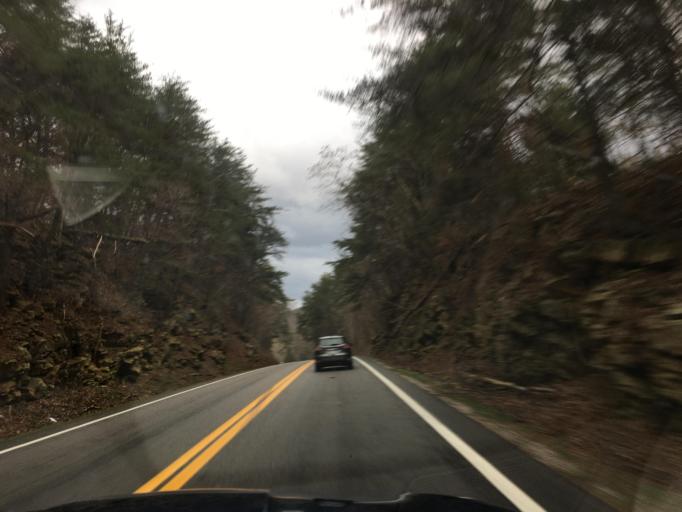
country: US
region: Tennessee
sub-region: Cumberland County
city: Crossville
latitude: 35.8794
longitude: -84.9354
